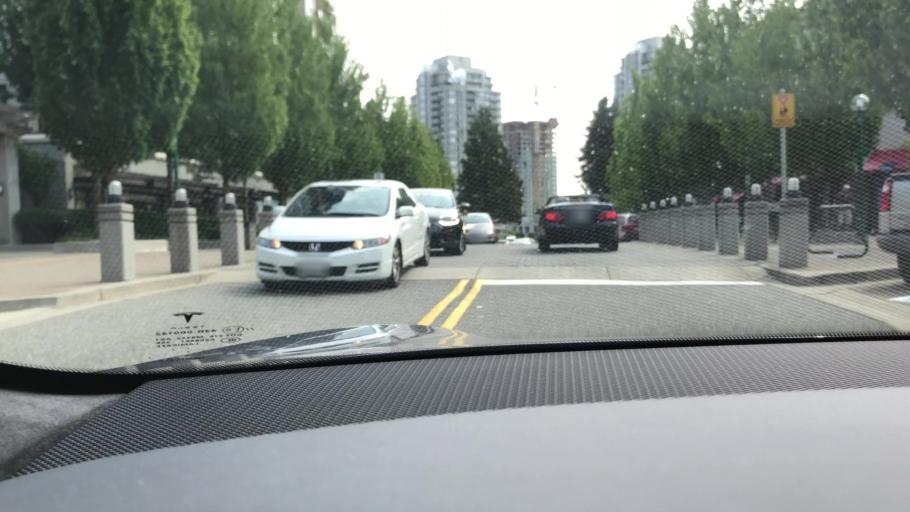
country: CA
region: British Columbia
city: Burnaby
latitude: 49.2193
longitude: -122.9565
